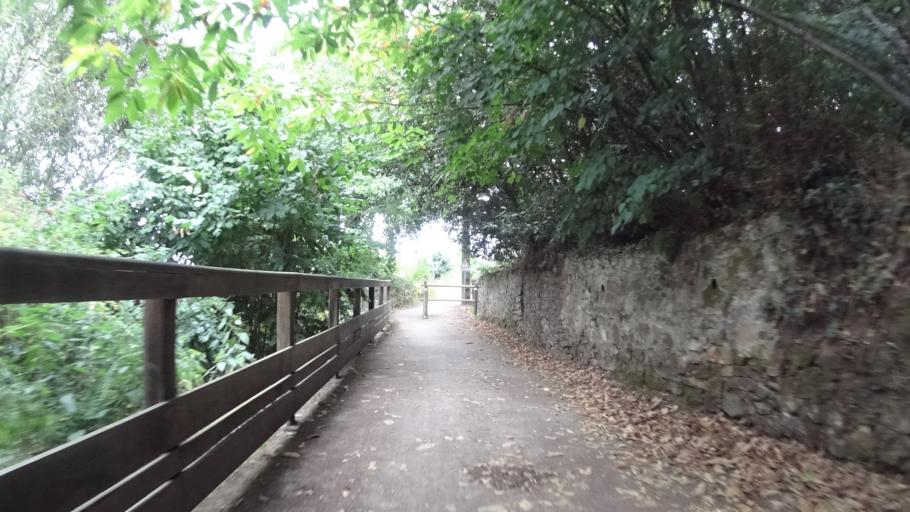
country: FR
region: Pays de la Loire
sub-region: Departement de la Loire-Atlantique
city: Le Pellerin
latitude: 47.2052
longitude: -1.7684
